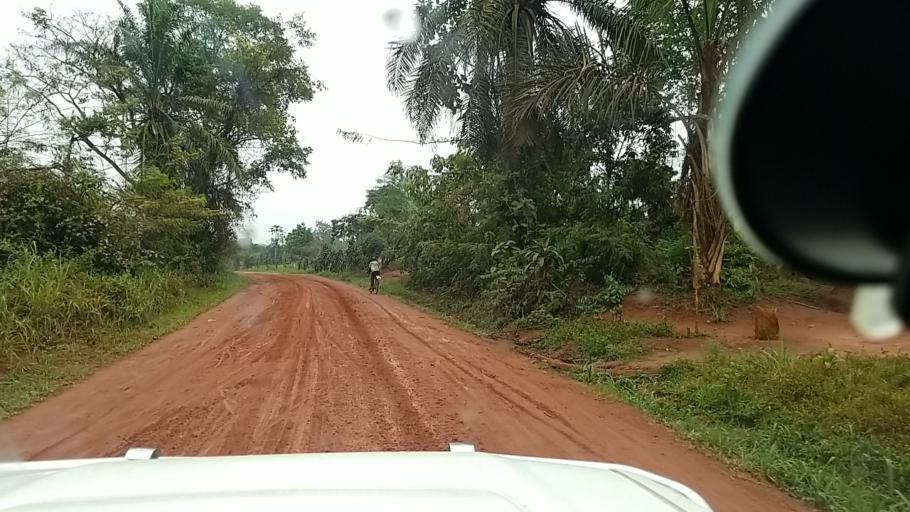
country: CD
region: Equateur
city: Gemena
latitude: 3.1115
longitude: 19.8263
